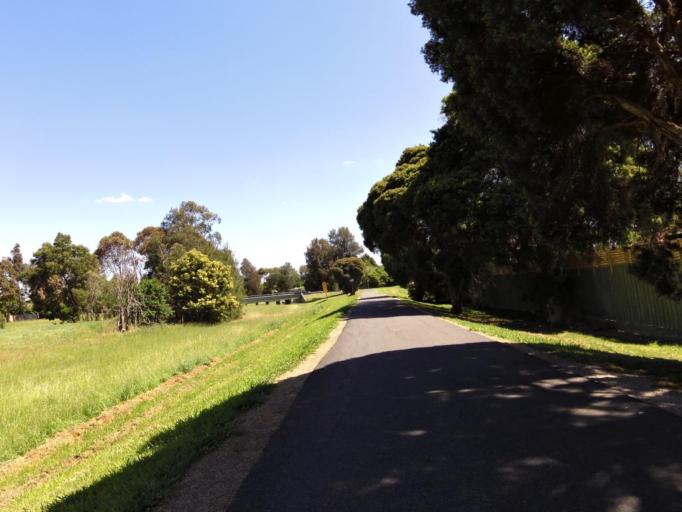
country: AU
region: Victoria
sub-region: Knox
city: Knoxfield
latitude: -37.8924
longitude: 145.2718
